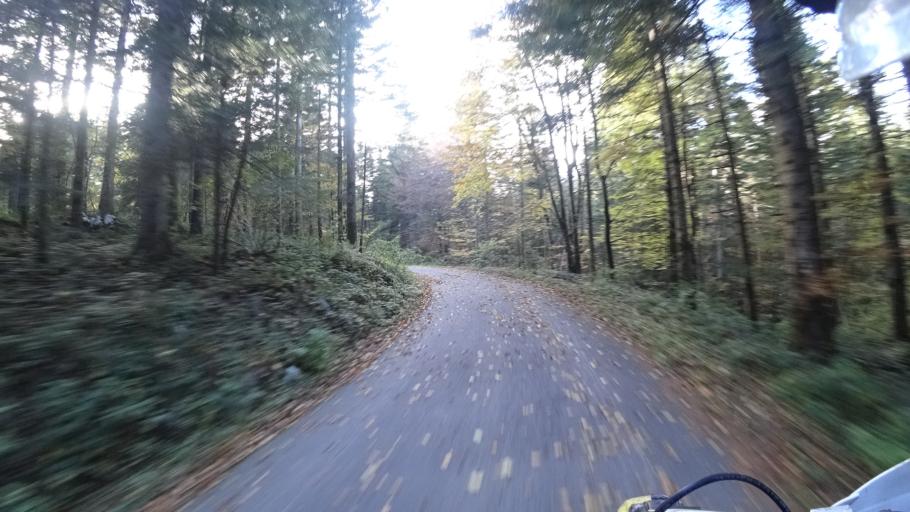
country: HR
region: Karlovacka
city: Plaski
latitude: 44.9827
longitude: 15.4064
